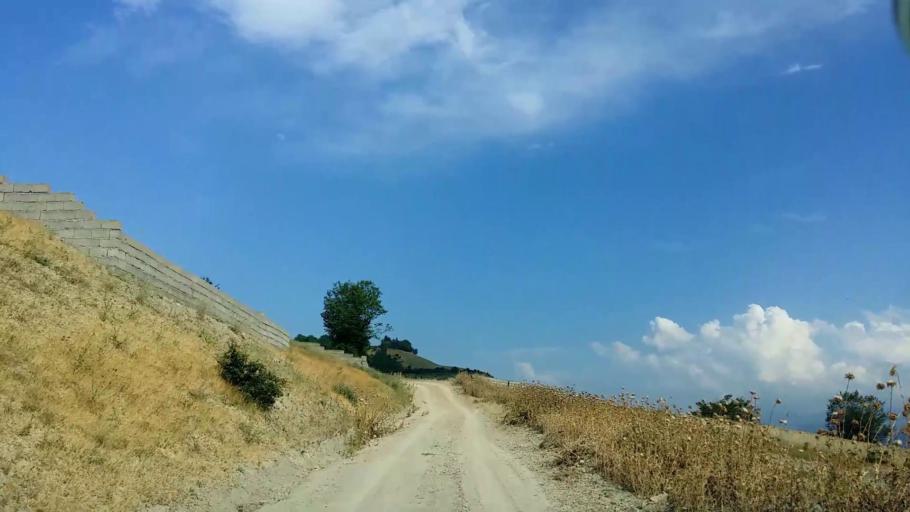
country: IR
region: Mazandaran
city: Chalus
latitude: 36.5463
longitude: 51.2964
